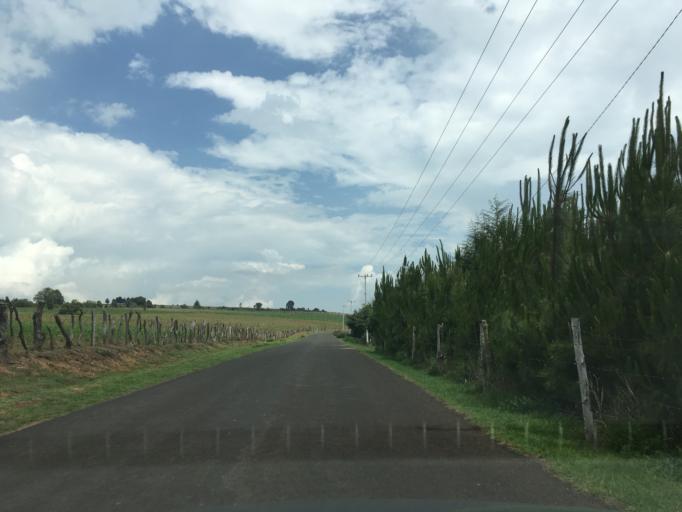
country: MX
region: Michoacan
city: Acuitzio del Canje
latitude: 19.5182
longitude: -101.2507
